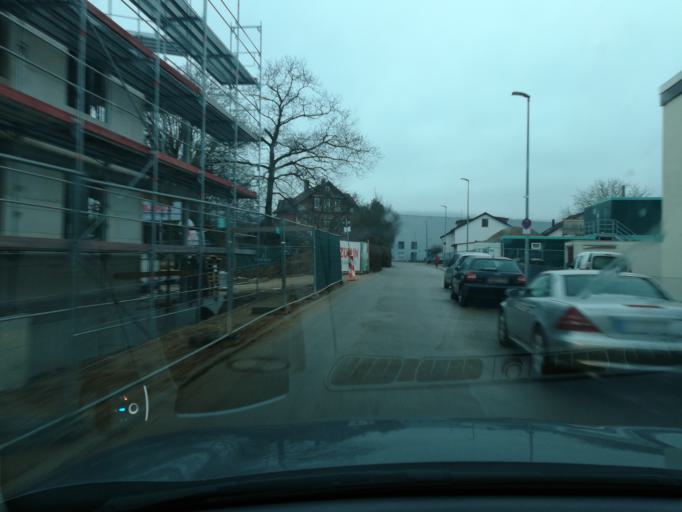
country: DE
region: Baden-Wuerttemberg
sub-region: Regierungsbezirk Stuttgart
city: Schorndorf
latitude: 48.8080
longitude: 9.5209
